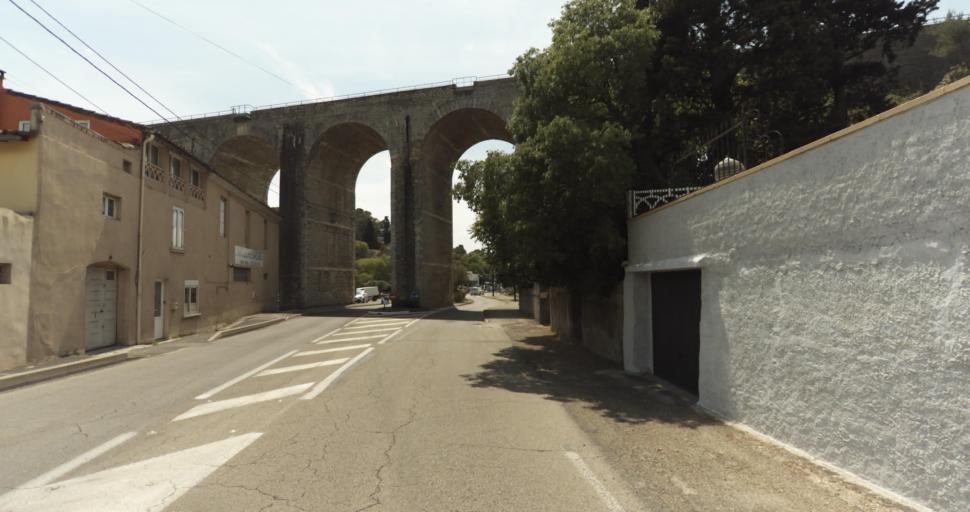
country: FR
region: Languedoc-Roussillon
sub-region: Departement du Gard
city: Nimes
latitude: 43.8488
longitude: 4.3465
